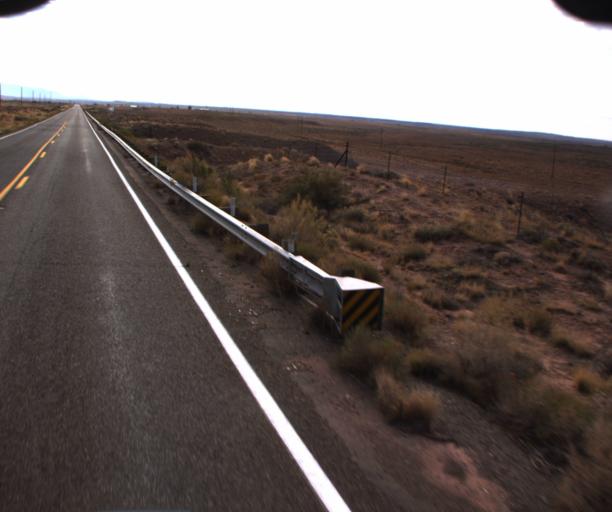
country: US
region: Arizona
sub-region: Apache County
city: Many Farms
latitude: 36.5238
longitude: -109.4961
